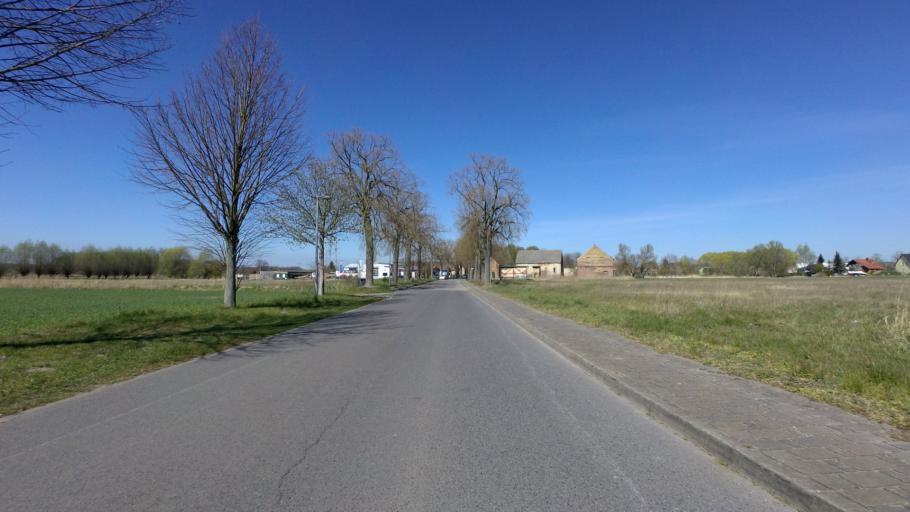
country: DE
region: Brandenburg
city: Rangsdorf
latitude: 52.3211
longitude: 13.4681
